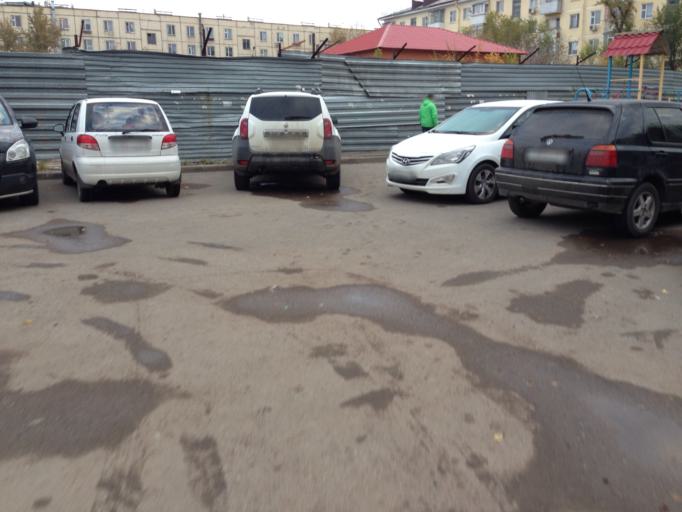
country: KZ
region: Astana Qalasy
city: Astana
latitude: 51.1876
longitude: 71.4166
